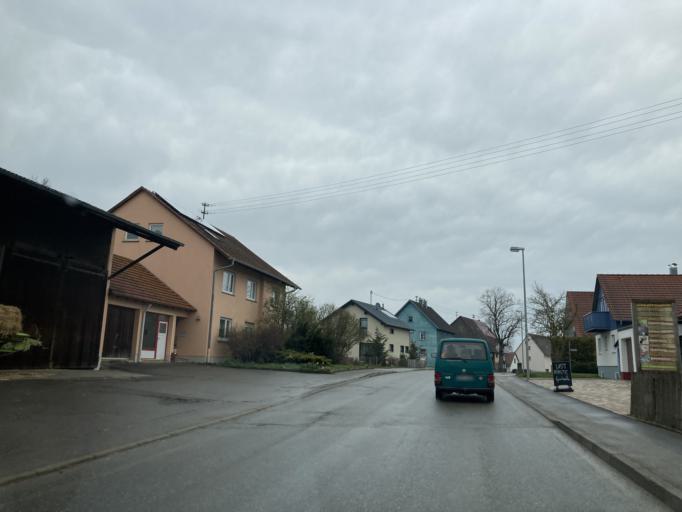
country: DE
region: Baden-Wuerttemberg
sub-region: Freiburg Region
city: Seedorf
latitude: 48.2662
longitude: 8.4800
